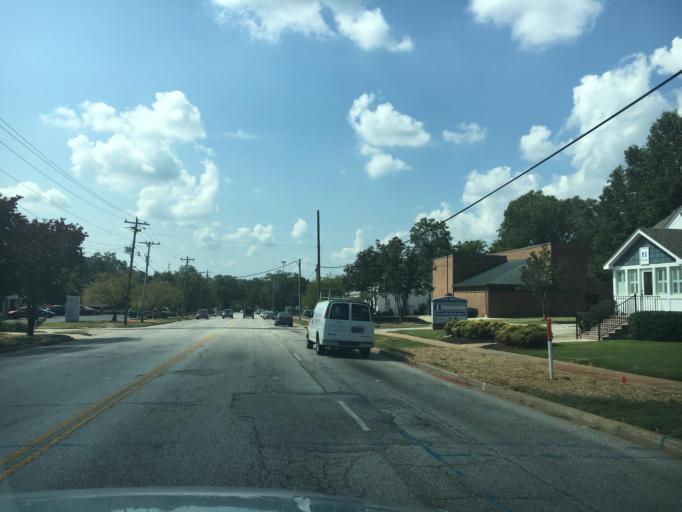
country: US
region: South Carolina
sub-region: Greenville County
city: Dunean
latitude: 34.8305
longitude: -82.4065
